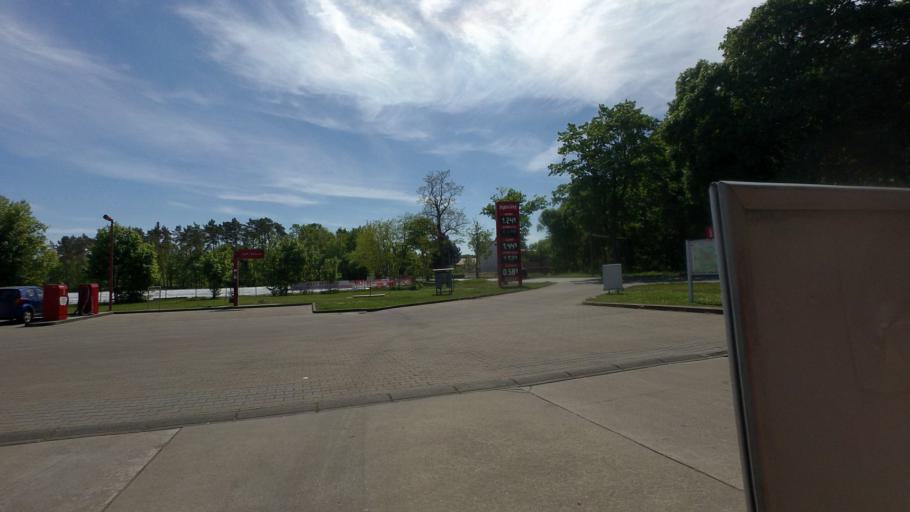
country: DE
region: Brandenburg
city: Luckenwalde
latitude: 52.1111
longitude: 13.1441
